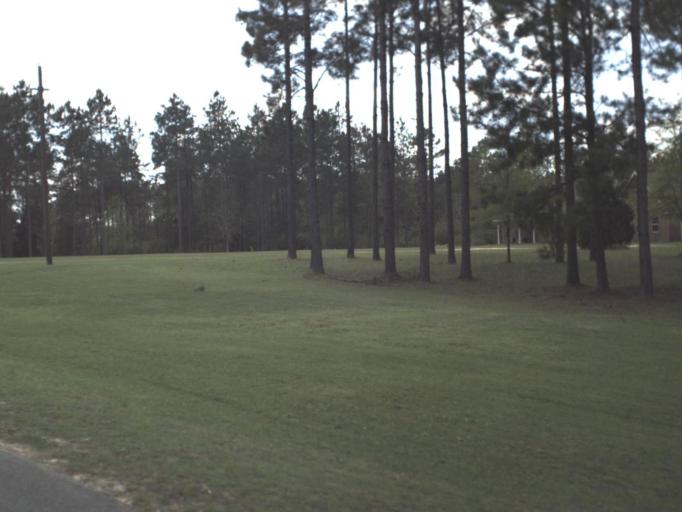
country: US
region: Florida
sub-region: Okaloosa County
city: Crestview
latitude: 30.9328
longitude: -86.6356
